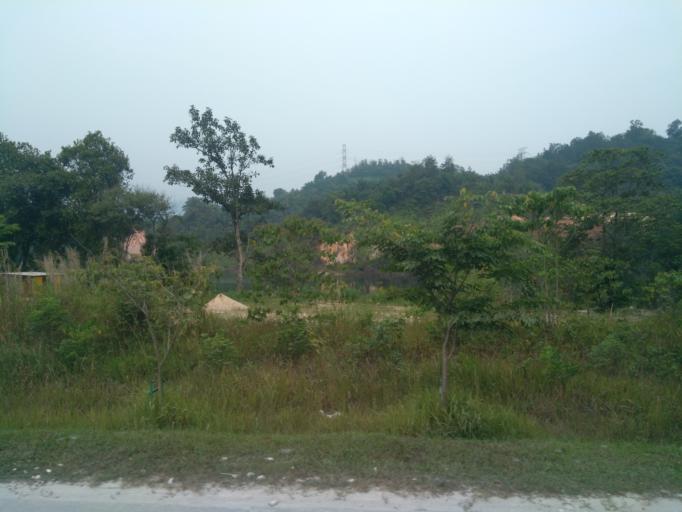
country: MY
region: Perak
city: Ipoh
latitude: 4.5504
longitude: 101.1633
